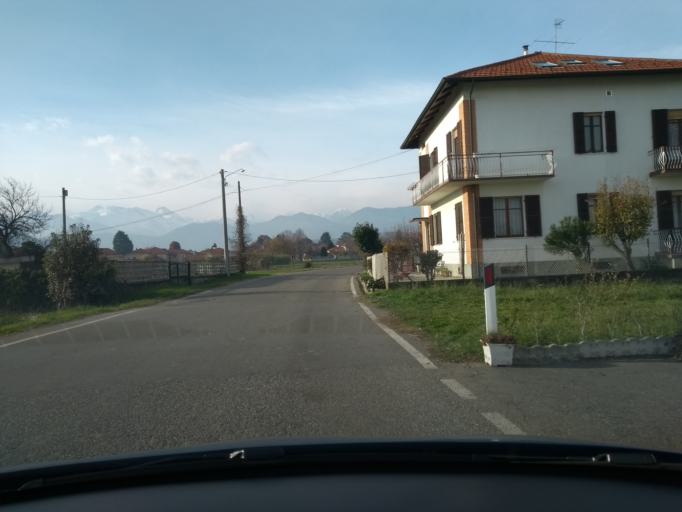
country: IT
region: Piedmont
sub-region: Provincia di Torino
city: Balangero
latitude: 45.2685
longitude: 7.5253
